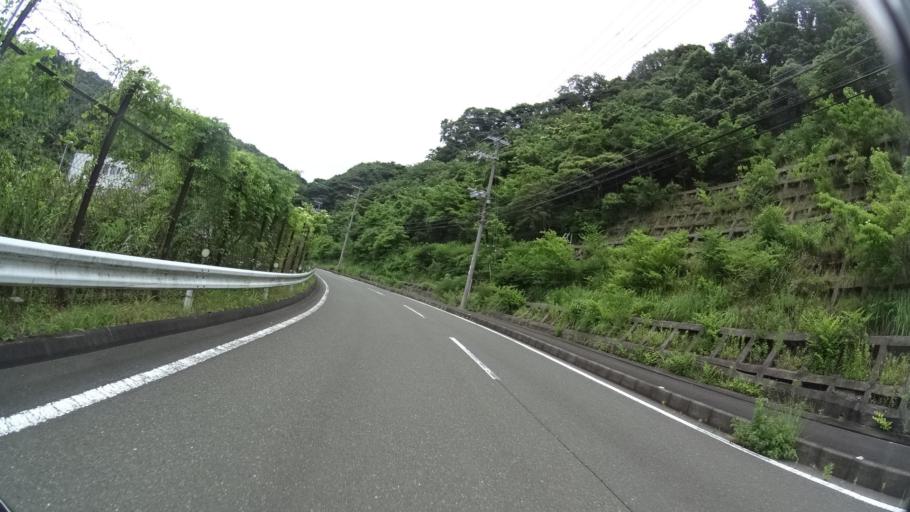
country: JP
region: Kyoto
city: Maizuru
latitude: 35.5265
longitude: 135.3458
